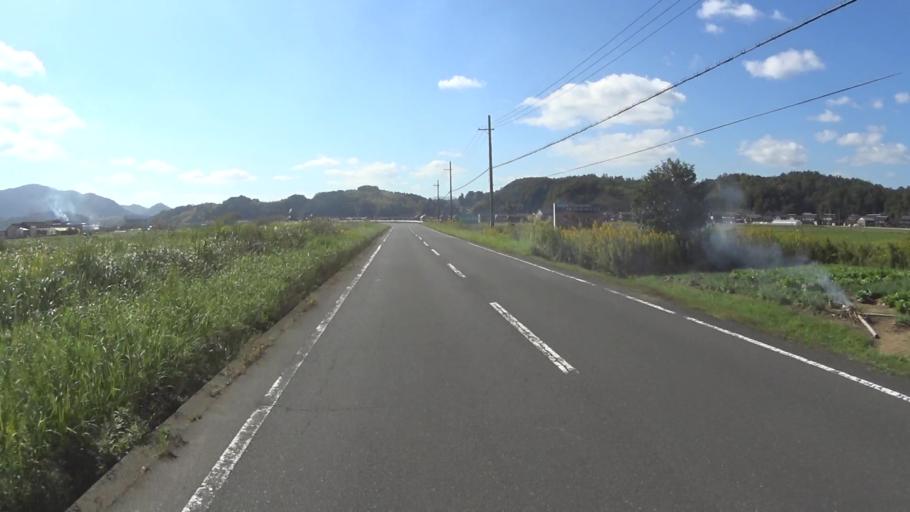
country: JP
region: Kyoto
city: Miyazu
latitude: 35.6671
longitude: 135.0864
